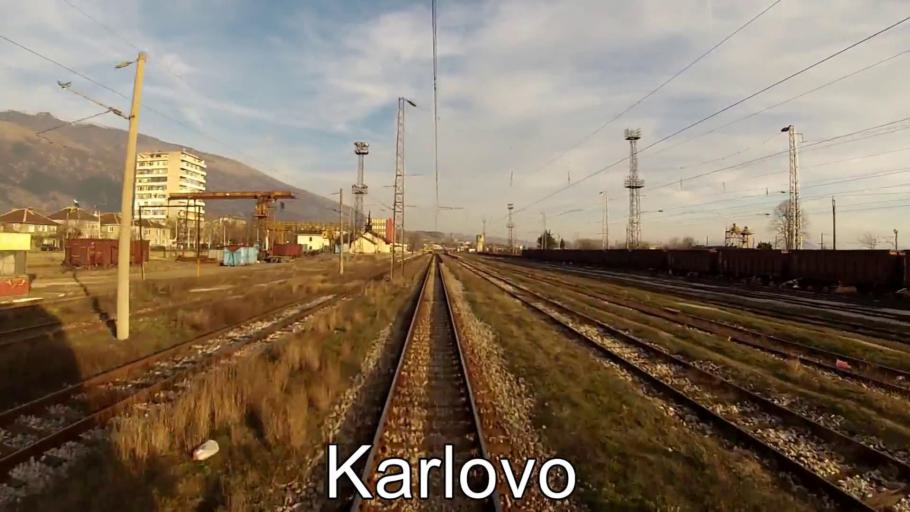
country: BG
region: Plovdiv
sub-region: Obshtina Karlovo
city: Karlovo
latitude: 42.6316
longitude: 24.7965
